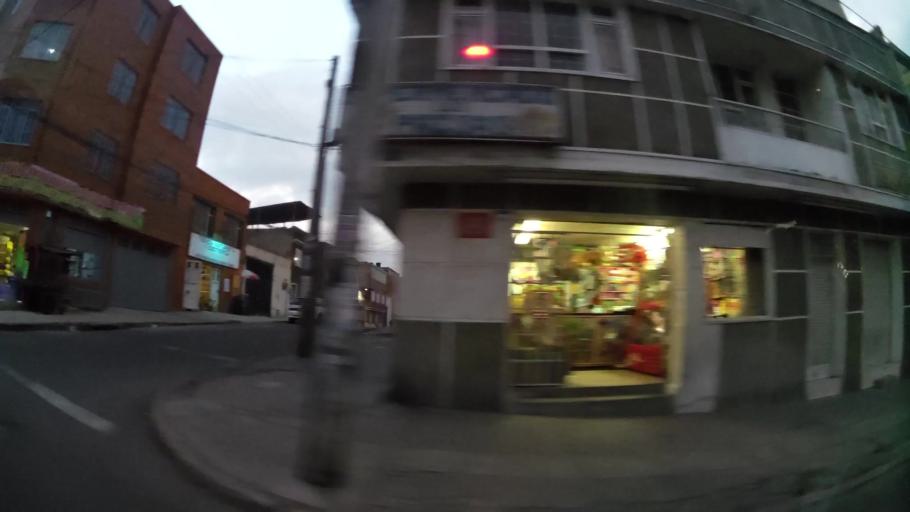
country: CO
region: Bogota D.C.
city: Bogota
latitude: 4.5823
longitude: -74.1334
